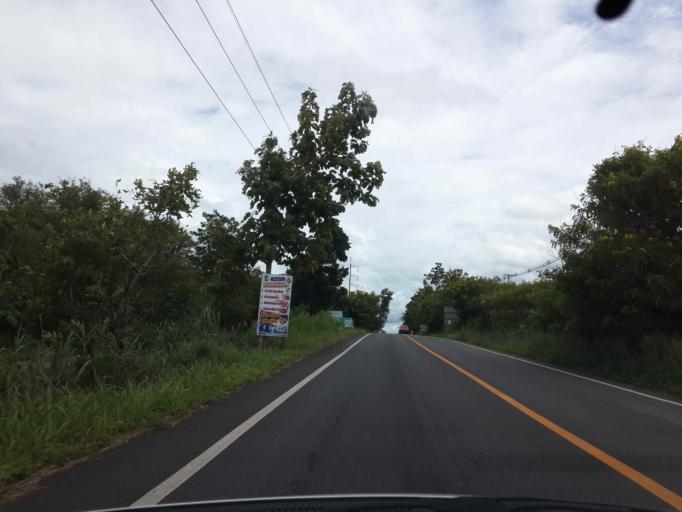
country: TH
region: Ratchaburi
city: Suan Phueng
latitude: 13.5480
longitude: 99.4660
